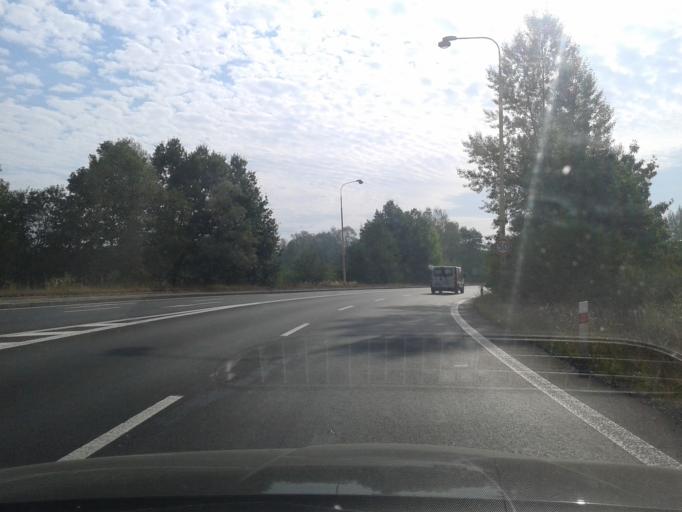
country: CZ
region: Moravskoslezsky
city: Havirov
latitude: 49.8031
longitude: 18.4434
